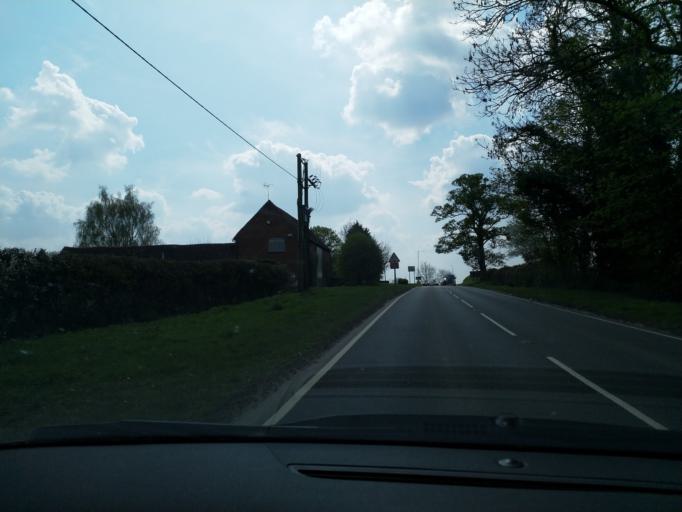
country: GB
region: England
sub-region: Warwickshire
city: Royal Leamington Spa
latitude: 52.3180
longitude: -1.5164
